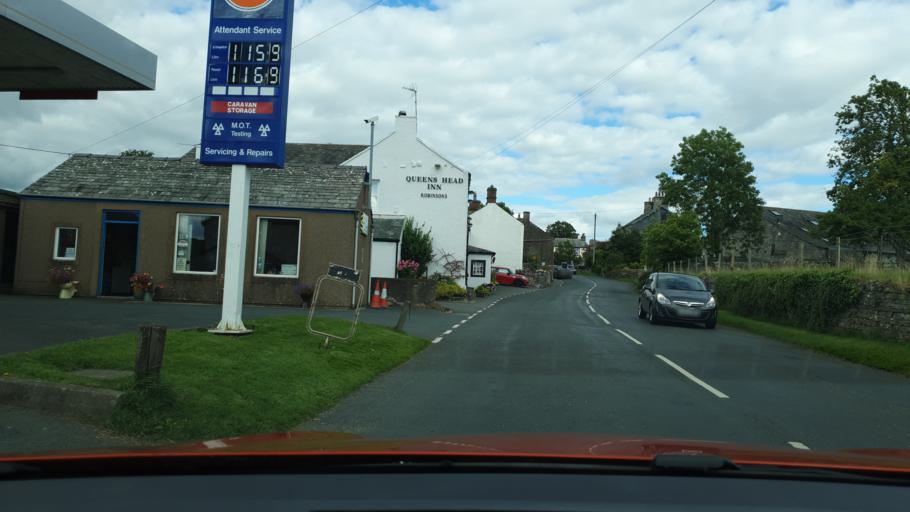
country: GB
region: England
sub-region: Cumbria
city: Penrith
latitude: 54.6327
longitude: -2.7728
